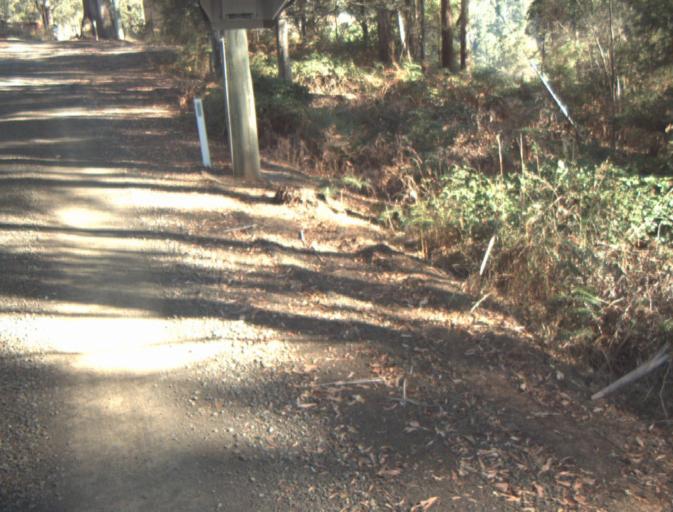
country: AU
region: Tasmania
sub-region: Launceston
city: Mayfield
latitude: -41.2938
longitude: 147.1973
